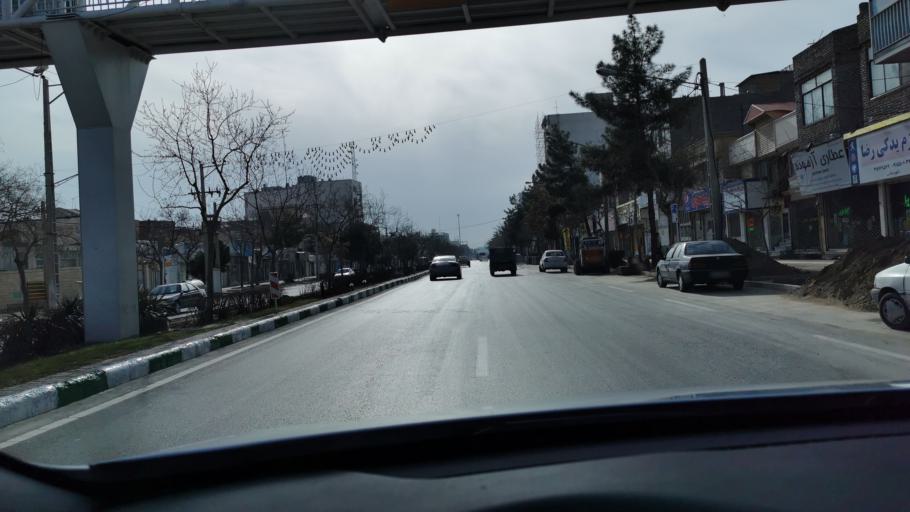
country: IR
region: Razavi Khorasan
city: Mashhad
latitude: 36.2928
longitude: 59.5345
